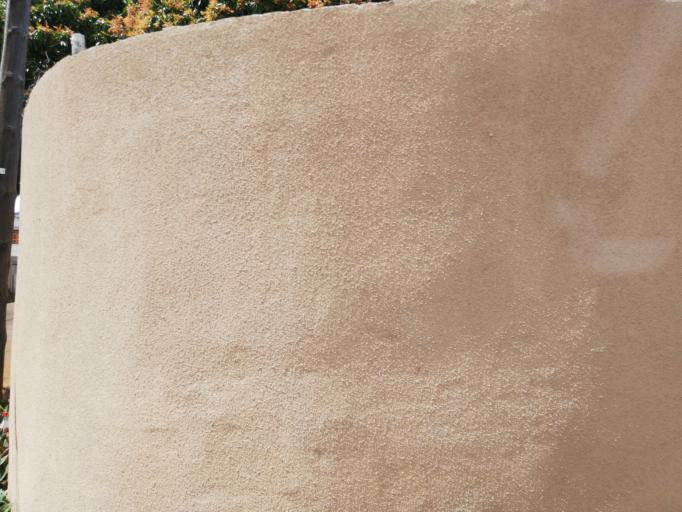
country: MU
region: Moka
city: Pailles
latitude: -20.2050
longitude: 57.4725
